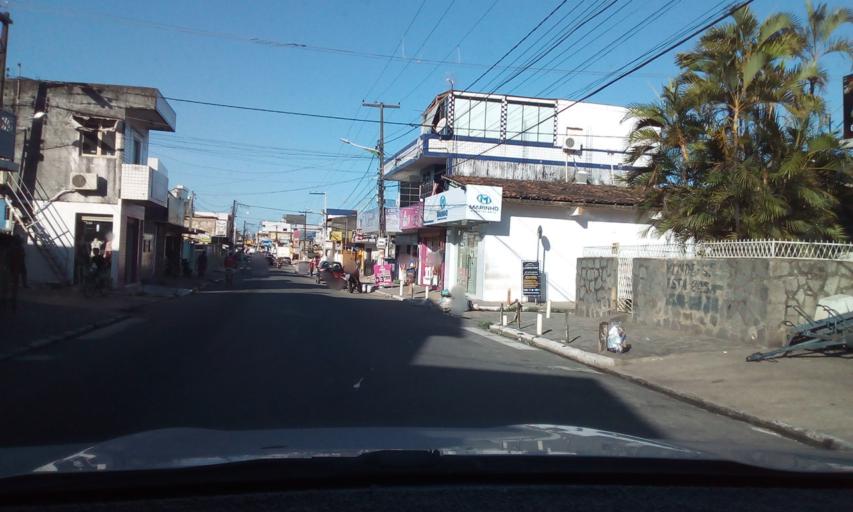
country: BR
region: Paraiba
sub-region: Bayeux
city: Bayeux
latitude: -7.1303
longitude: -34.9310
